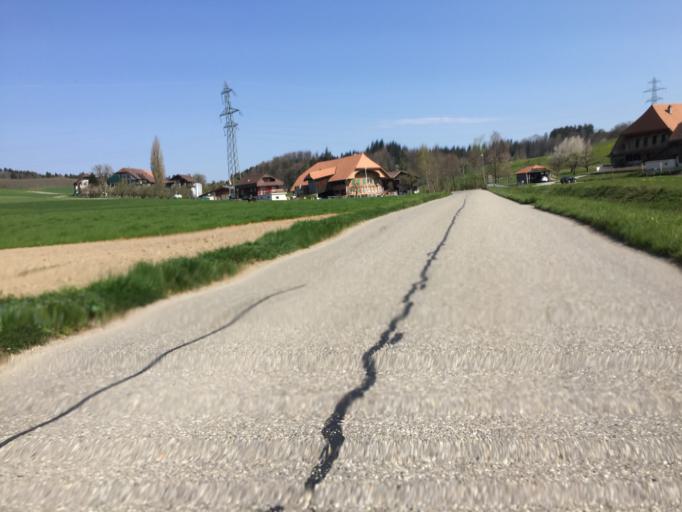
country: CH
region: Bern
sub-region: Bern-Mittelland District
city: Munchenbuchsee
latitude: 47.0344
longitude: 7.4540
